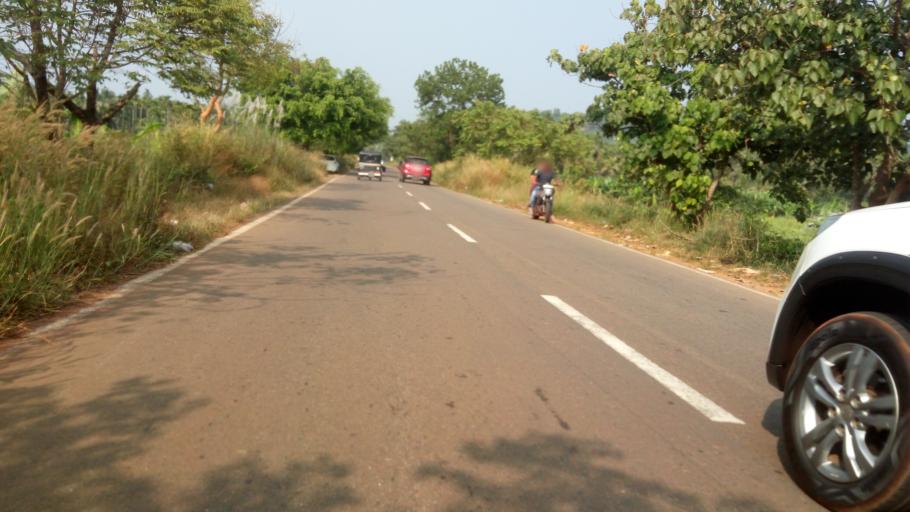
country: IN
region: Kerala
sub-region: Malappuram
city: Malappuram
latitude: 10.9964
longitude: 76.0145
